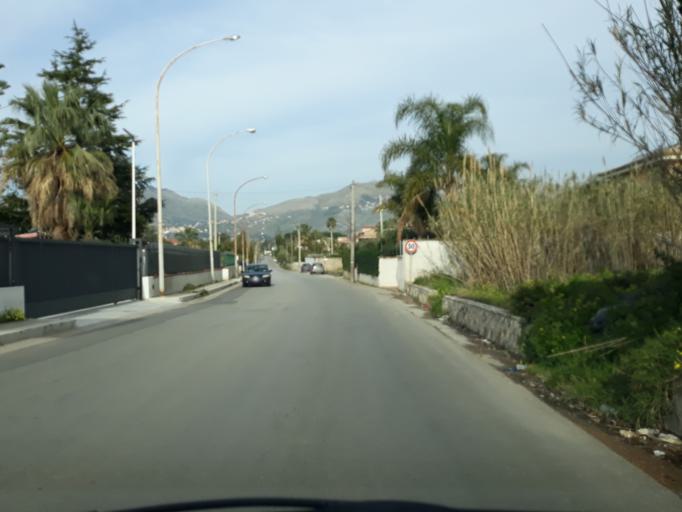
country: IT
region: Sicily
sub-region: Palermo
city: Borgetto
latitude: 38.0574
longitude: 13.1327
